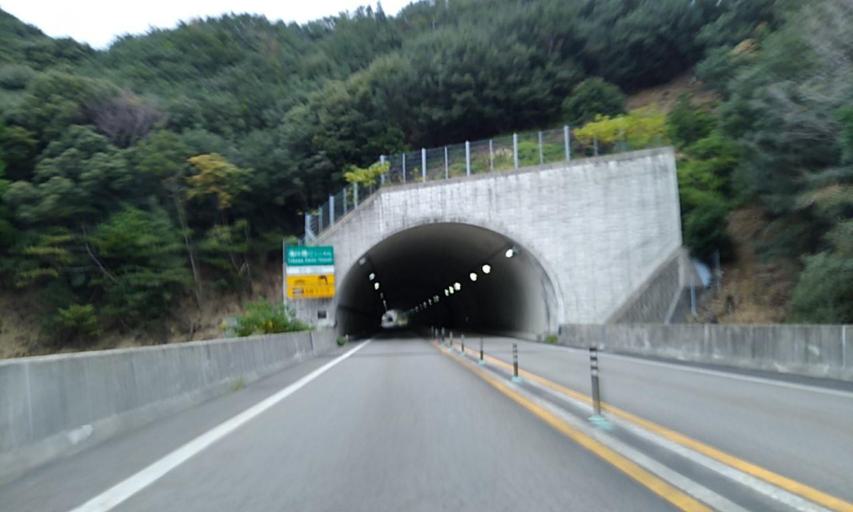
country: JP
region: Wakayama
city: Shingu
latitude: 33.6291
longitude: 135.9223
